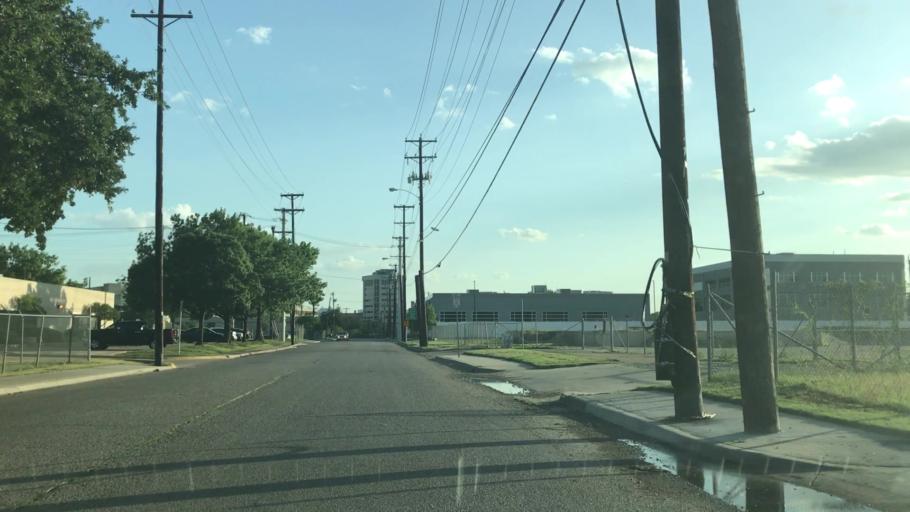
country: US
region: Texas
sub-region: Dallas County
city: Dallas
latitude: 32.8166
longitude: -96.8359
